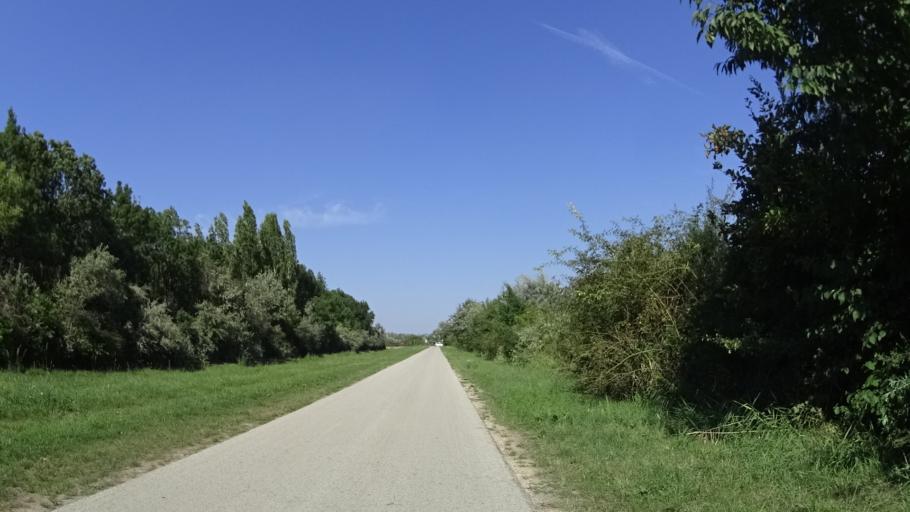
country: HU
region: Fejer
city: Gardony
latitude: 47.2256
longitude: 18.5926
